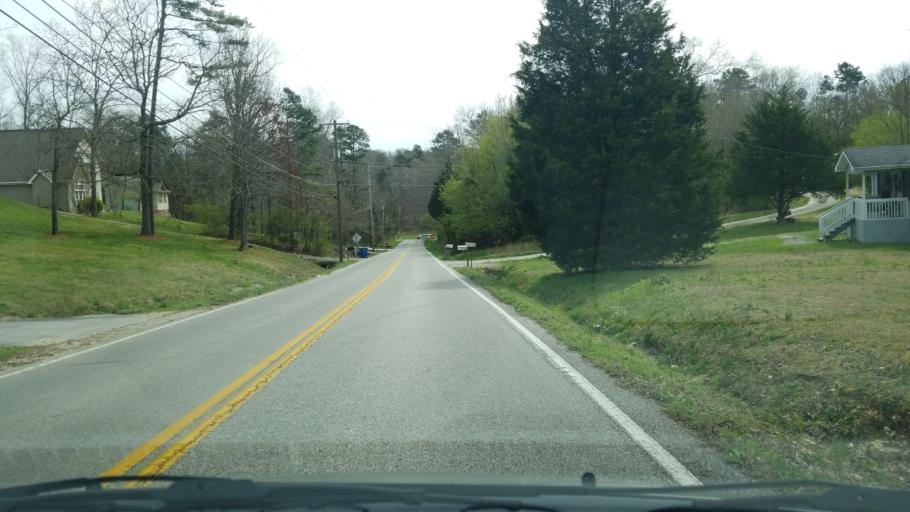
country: US
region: Tennessee
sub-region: Hamilton County
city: East Brainerd
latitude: 35.0155
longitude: -85.1154
